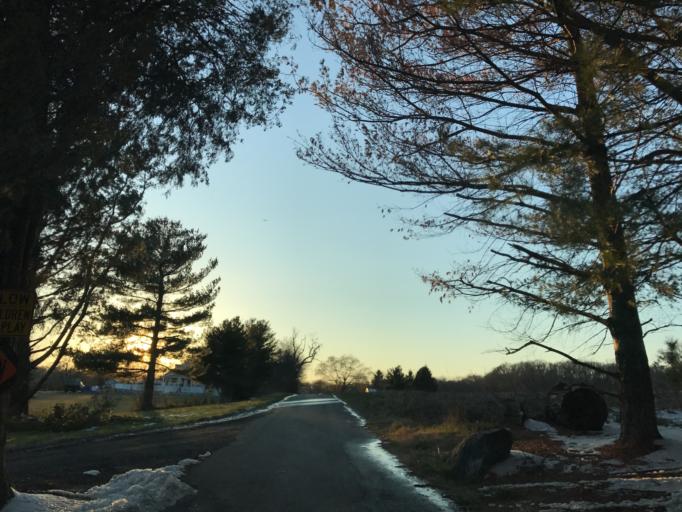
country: US
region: Maryland
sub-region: Baltimore County
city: Edgemere
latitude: 39.2755
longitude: -76.4007
